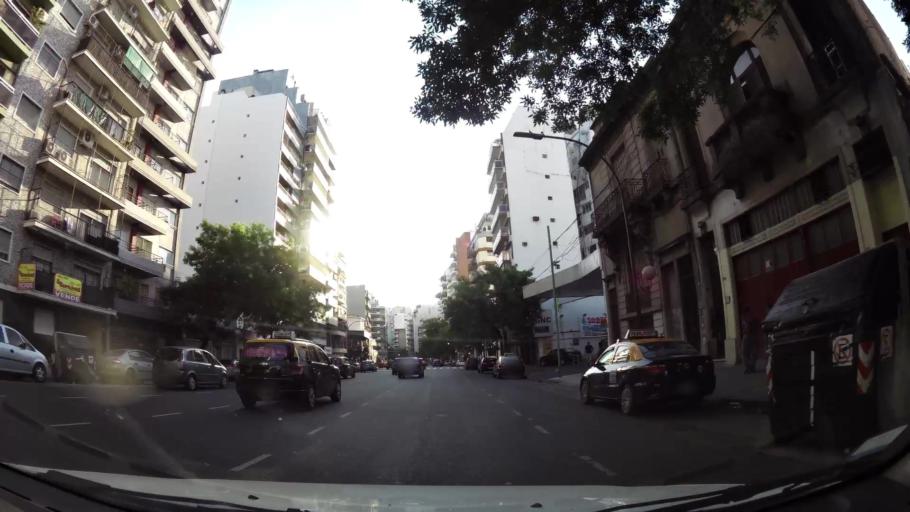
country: AR
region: Buenos Aires F.D.
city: Colegiales
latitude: -34.5982
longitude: -58.4272
